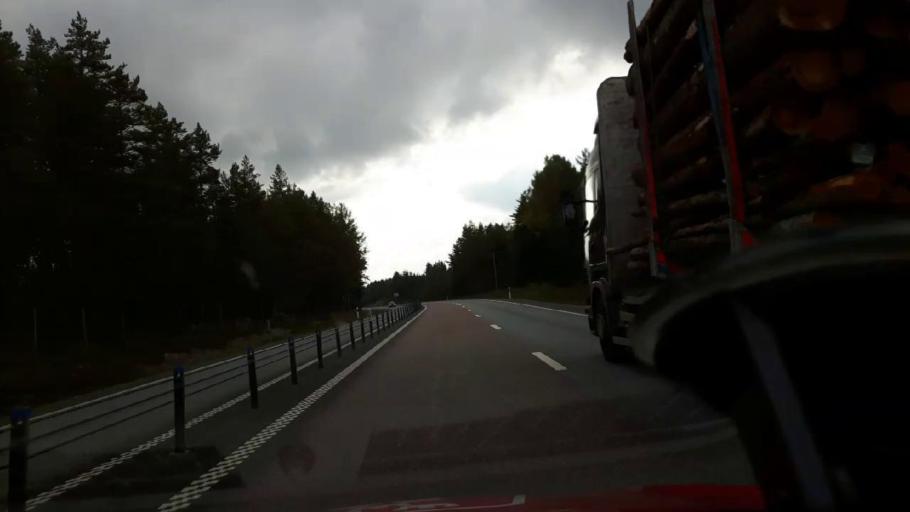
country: SE
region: Gaevleborg
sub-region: Gavle Kommun
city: Norrsundet
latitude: 61.0213
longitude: 16.9766
